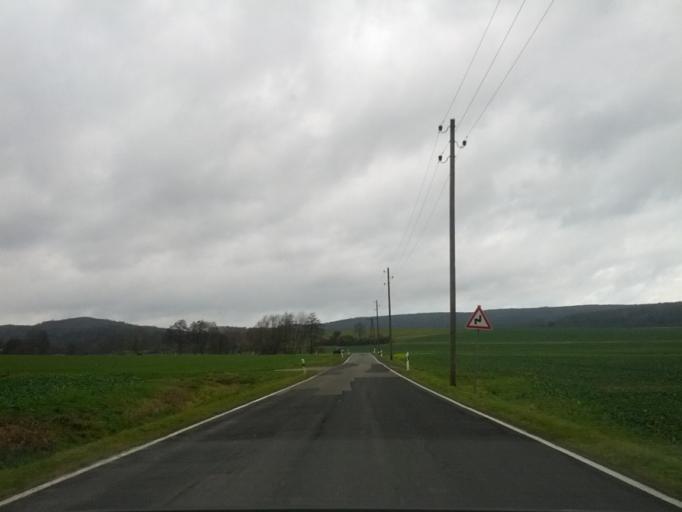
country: DE
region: Thuringia
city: Haina
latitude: 51.0184
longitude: 10.4780
